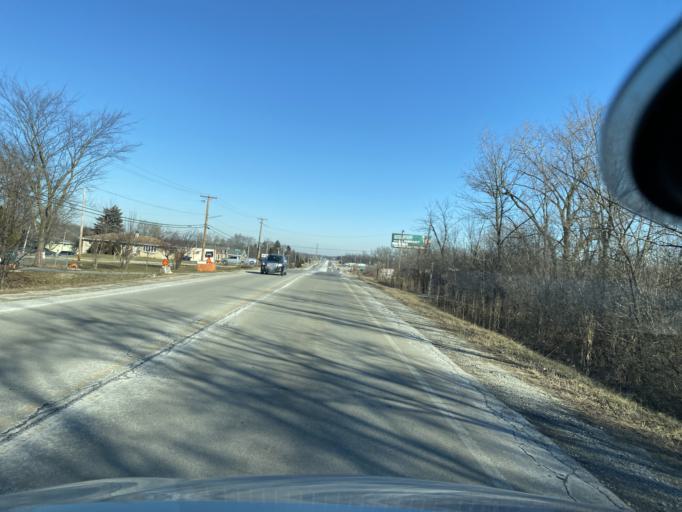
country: US
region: Illinois
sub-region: Will County
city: Lockport
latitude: 41.6241
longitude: -88.0254
